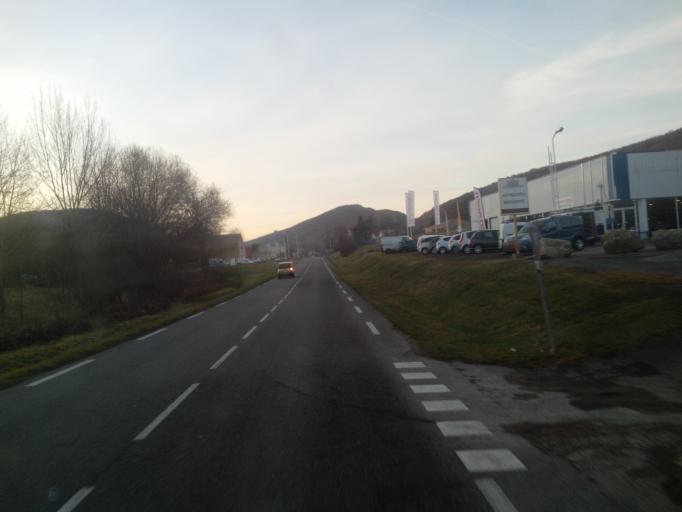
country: FR
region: Midi-Pyrenees
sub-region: Departement de l'Ariege
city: Lavelanet
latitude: 42.9244
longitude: 1.8667
